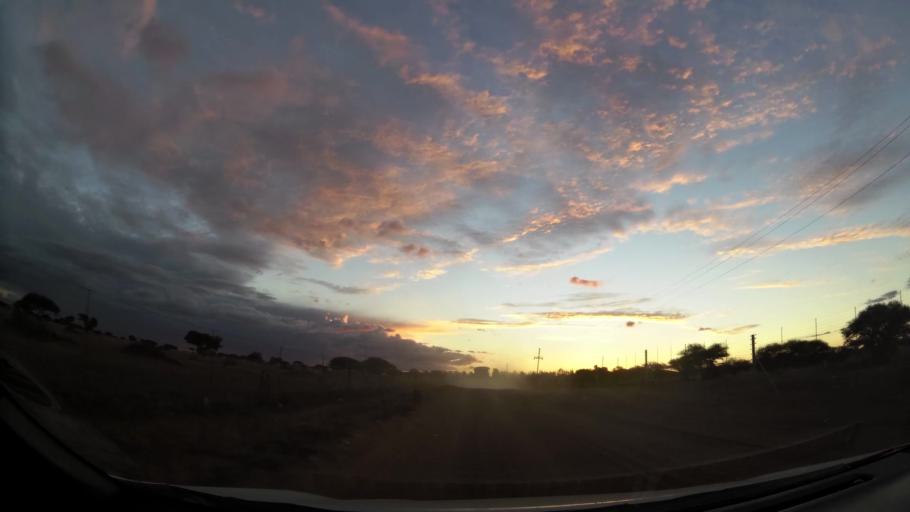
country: ZA
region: Limpopo
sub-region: Capricorn District Municipality
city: Polokwane
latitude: -23.7354
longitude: 29.4289
